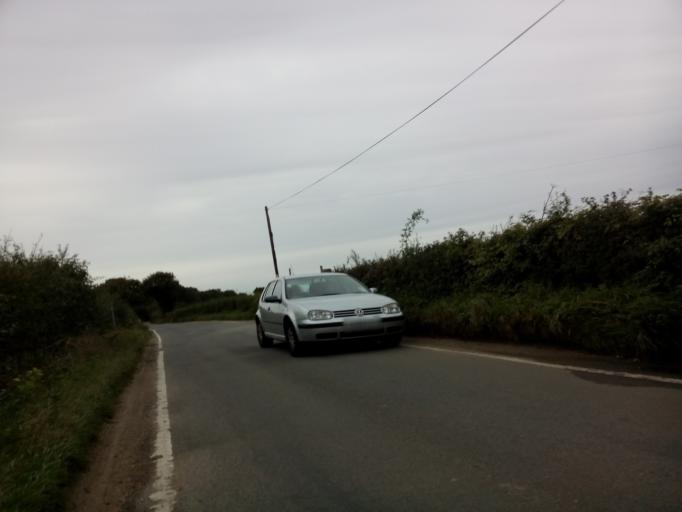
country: GB
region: England
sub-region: Suffolk
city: Ipswich
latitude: 52.0162
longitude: 1.1193
